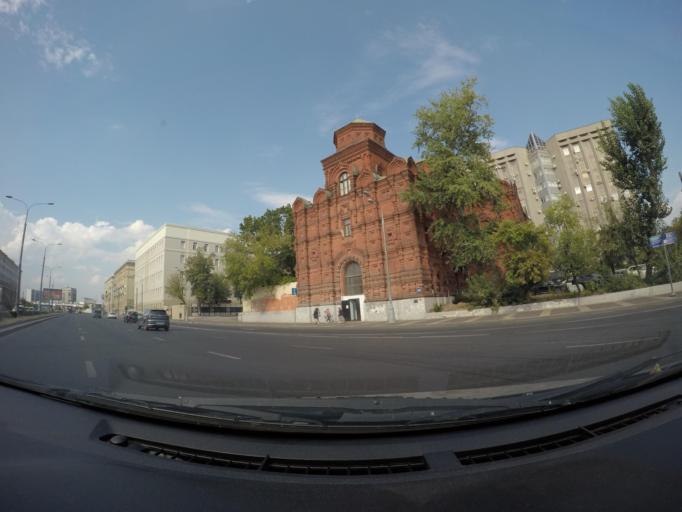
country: RU
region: Moscow
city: Mar'ina Roshcha
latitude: 55.7890
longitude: 37.5920
